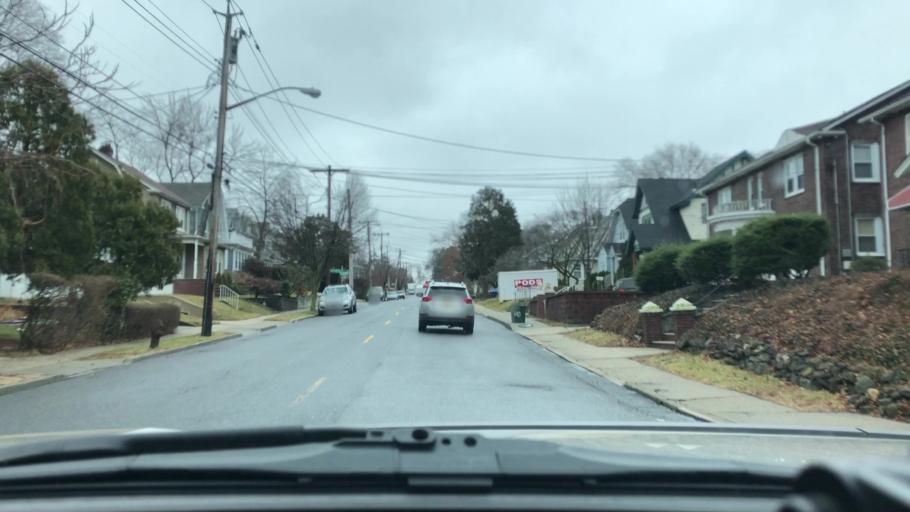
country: US
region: New Jersey
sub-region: Hudson County
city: Bayonne
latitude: 40.6279
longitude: -74.1053
